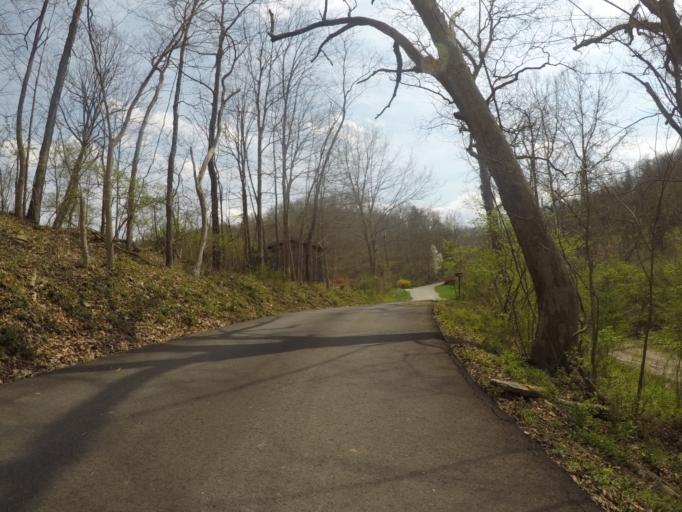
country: US
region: West Virginia
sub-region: Cabell County
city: Pea Ridge
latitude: 38.3931
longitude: -82.3490
